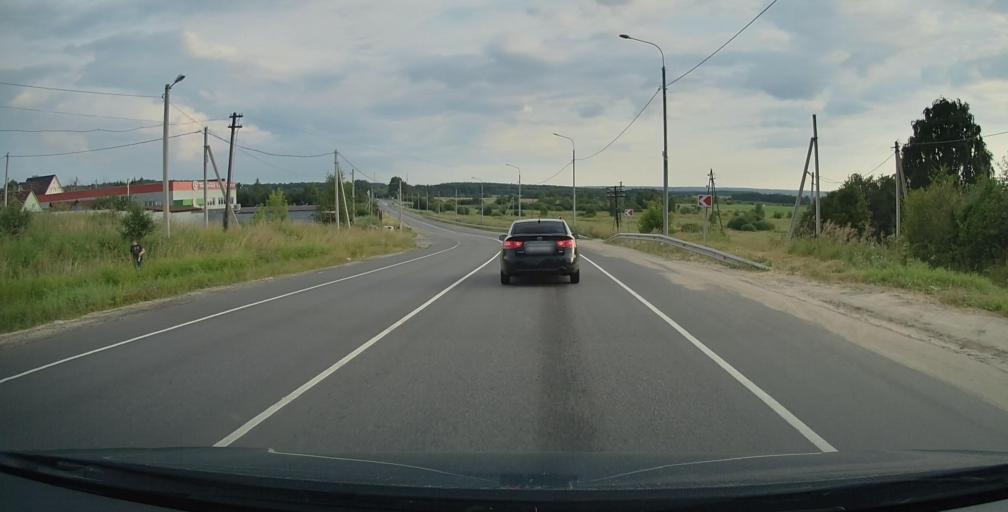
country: RU
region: Moskovskaya
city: Bogorodskoye
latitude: 56.5824
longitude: 38.1495
